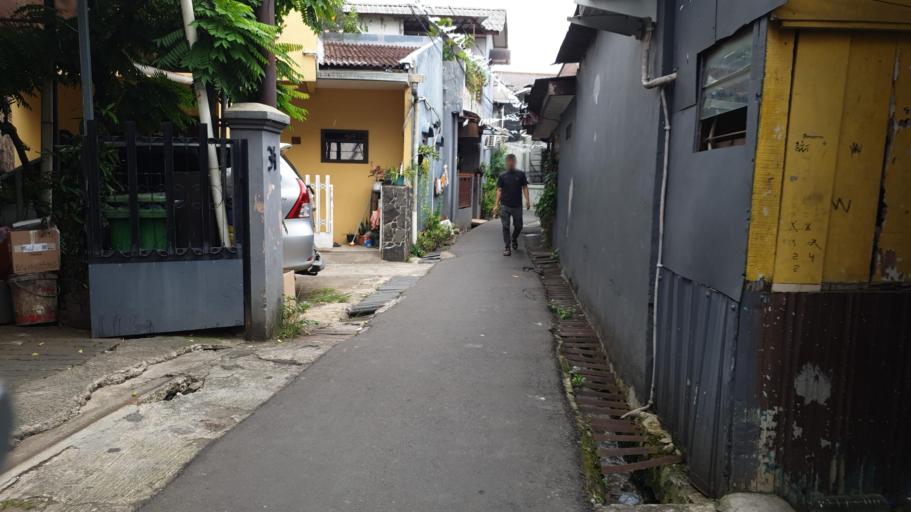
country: ID
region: Banten
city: South Tangerang
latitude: -6.2880
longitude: 106.7916
